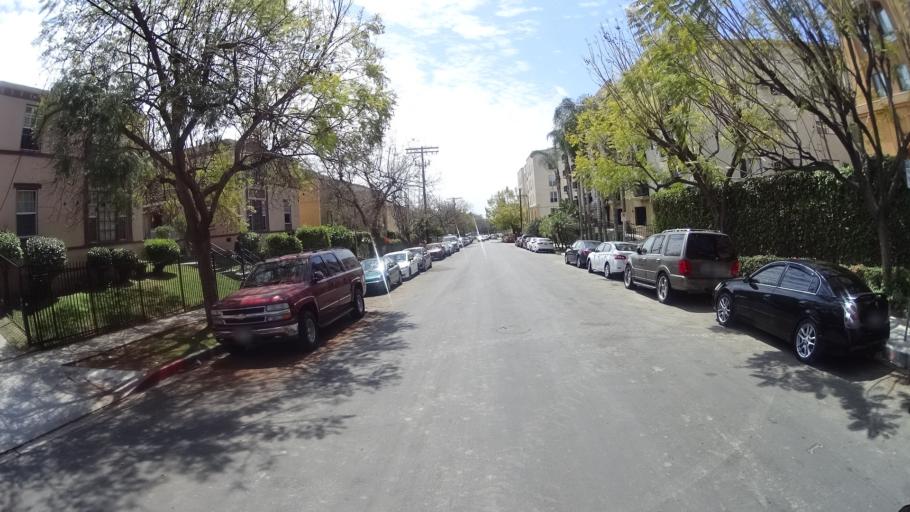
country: US
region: California
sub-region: Los Angeles County
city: Echo Park
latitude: 34.0581
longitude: -118.2652
